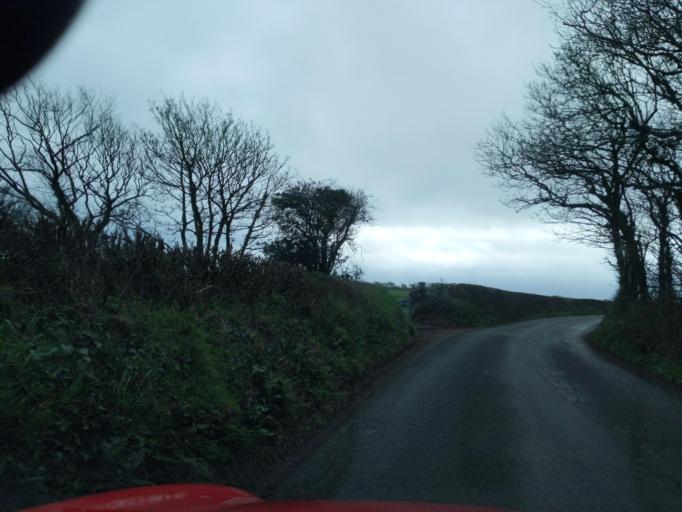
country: GB
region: England
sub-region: Devon
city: Wembury
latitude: 50.3322
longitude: -4.0935
